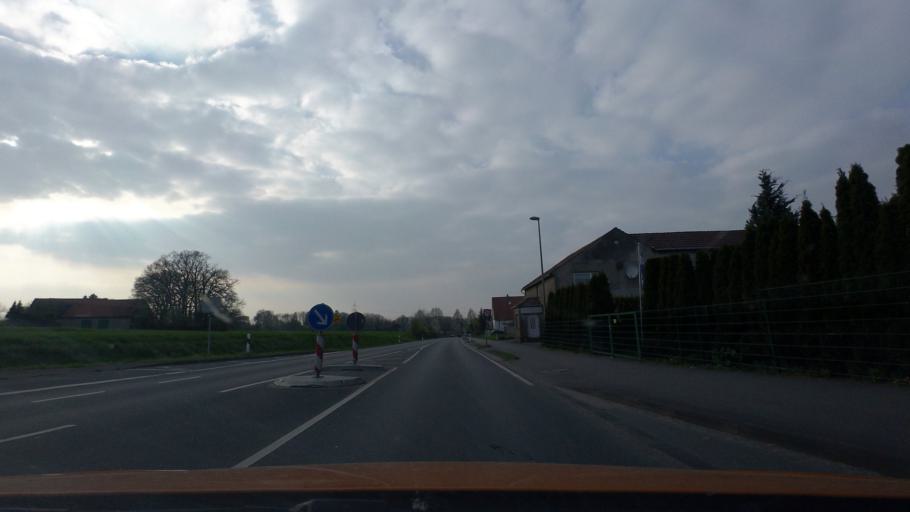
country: DE
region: North Rhine-Westphalia
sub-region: Regierungsbezirk Detmold
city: Hiddenhausen
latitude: 52.1300
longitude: 8.6229
